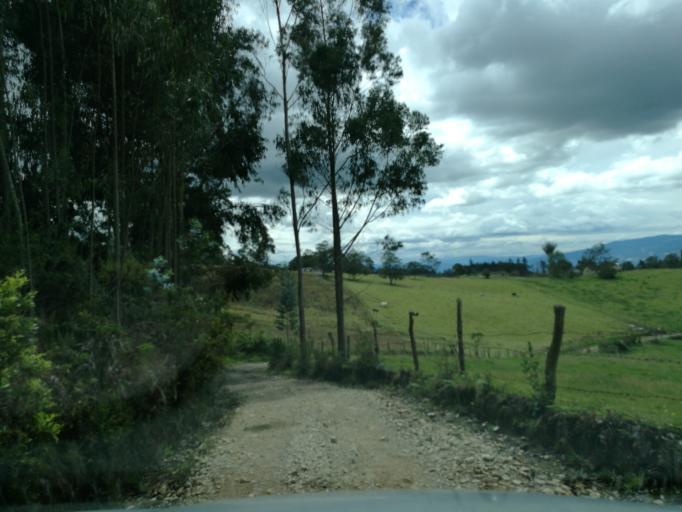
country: CO
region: Boyaca
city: Arcabuco
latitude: 5.7496
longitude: -73.4628
